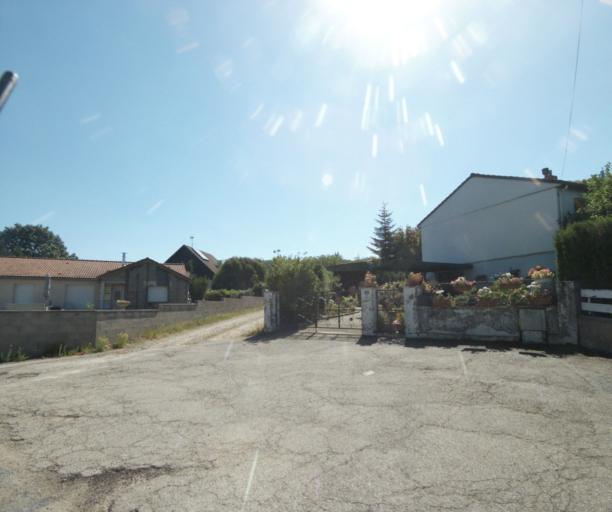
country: FR
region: Lorraine
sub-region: Departement des Vosges
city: Epinal
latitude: 48.1777
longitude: 6.4810
